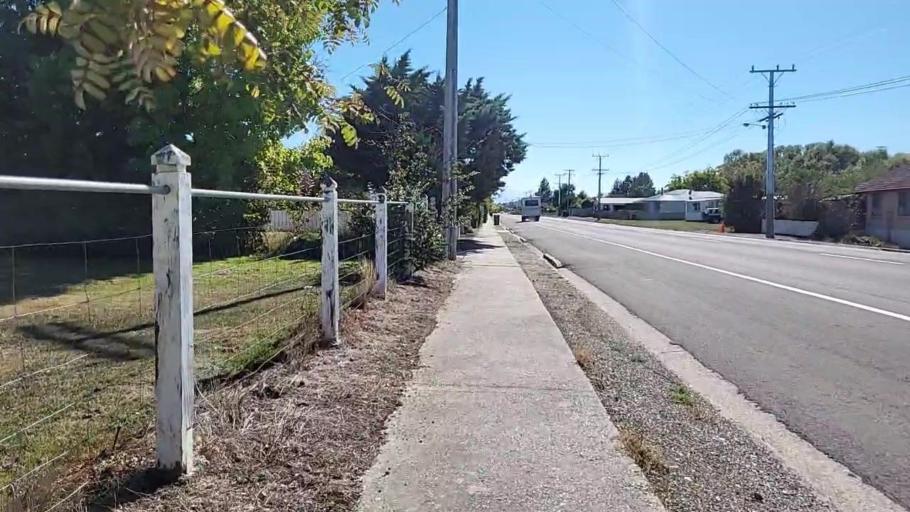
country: NZ
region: Otago
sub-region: Queenstown-Lakes District
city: Wanaka
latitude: -45.1038
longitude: 169.5951
